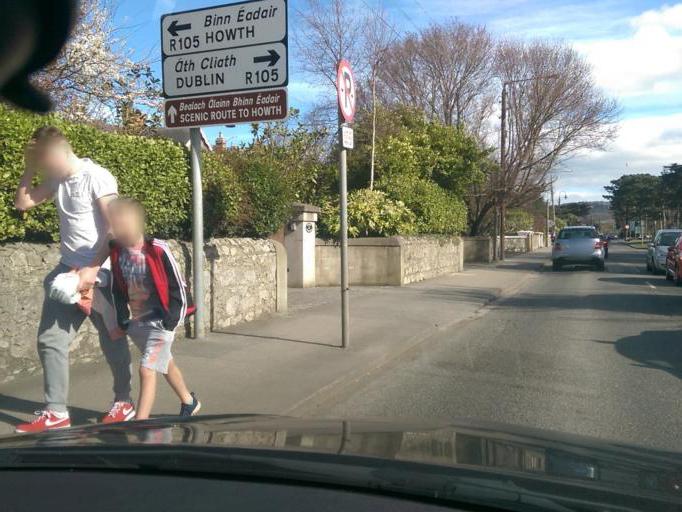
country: IE
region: Leinster
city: Sutton
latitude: 53.3902
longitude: -6.1123
